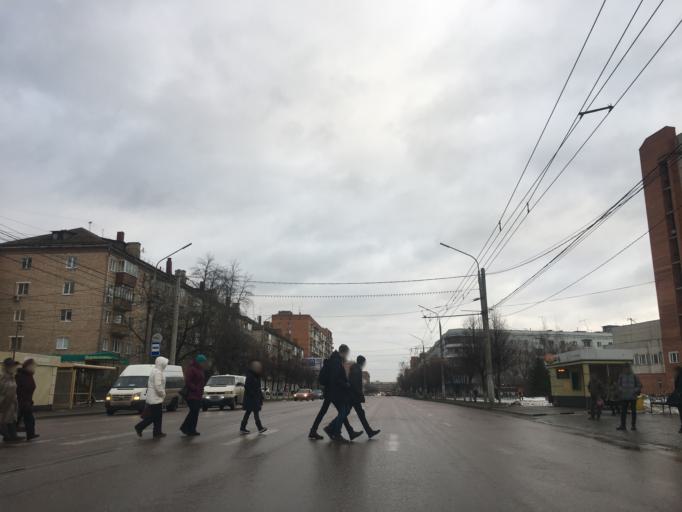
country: RU
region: Tula
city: Tula
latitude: 54.1975
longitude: 37.5954
